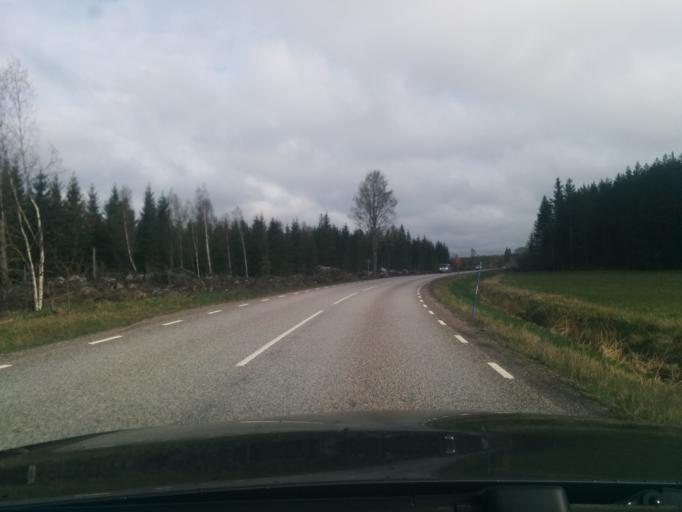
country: SE
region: Uppsala
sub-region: Tierps Kommun
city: Orbyhus
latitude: 60.2059
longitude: 17.6986
